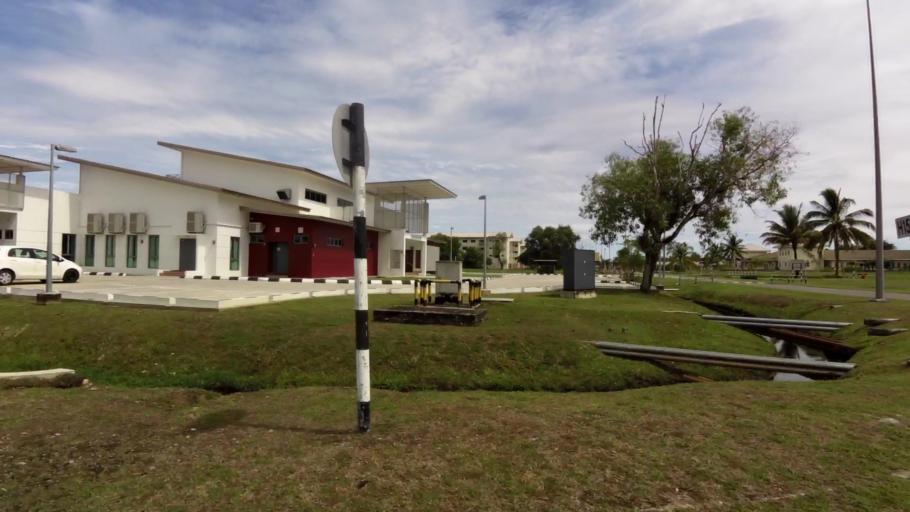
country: BN
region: Belait
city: Seria
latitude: 4.6023
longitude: 114.3138
